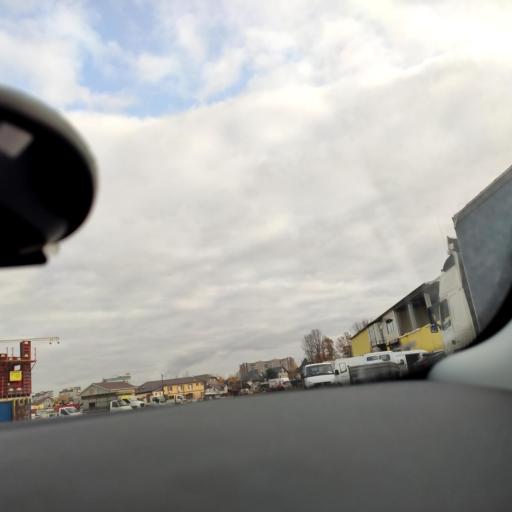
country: RU
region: Moskovskaya
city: Mosrentgen
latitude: 55.6241
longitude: 37.4640
